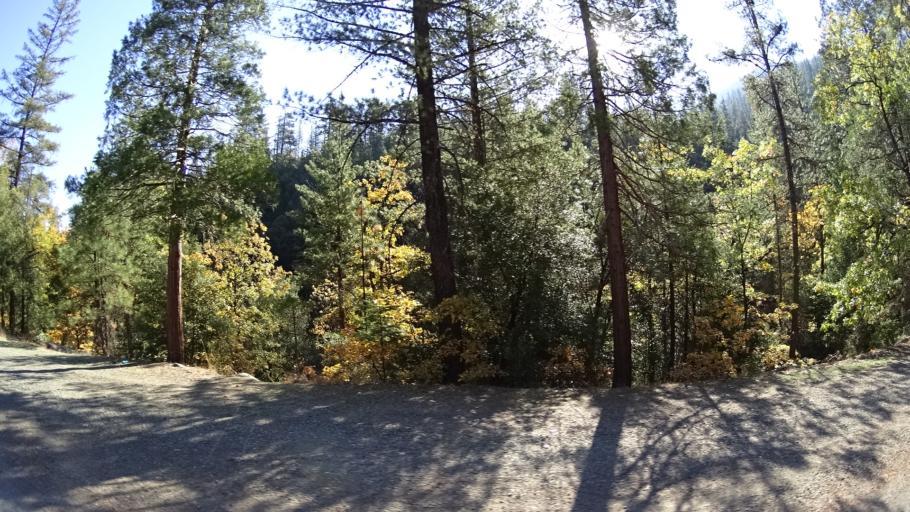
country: US
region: California
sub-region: Siskiyou County
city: Happy Camp
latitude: 41.6844
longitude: -123.0906
